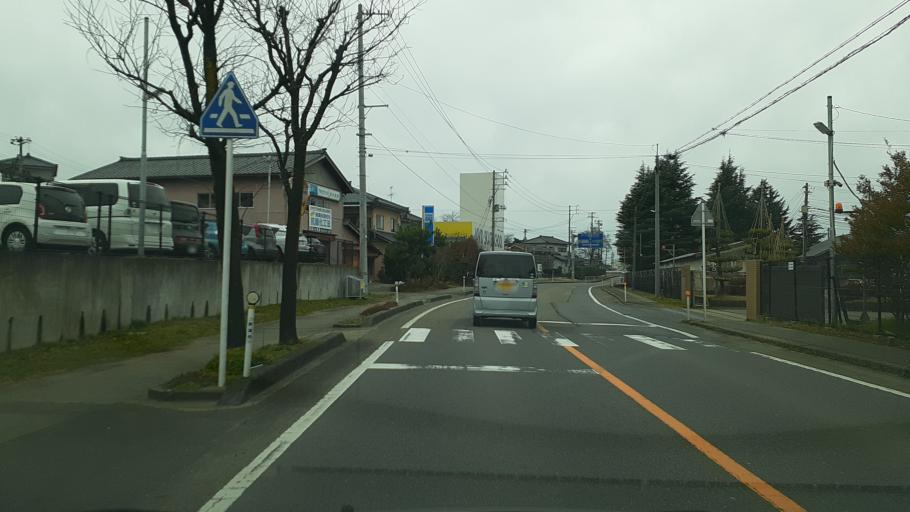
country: JP
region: Niigata
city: Niitsu-honcho
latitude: 37.7940
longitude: 139.1337
